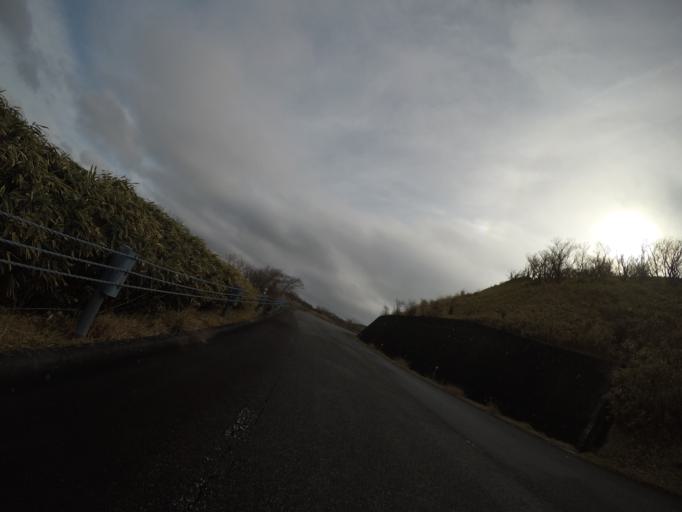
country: JP
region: Shizuoka
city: Heda
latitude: 34.8656
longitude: 138.8413
